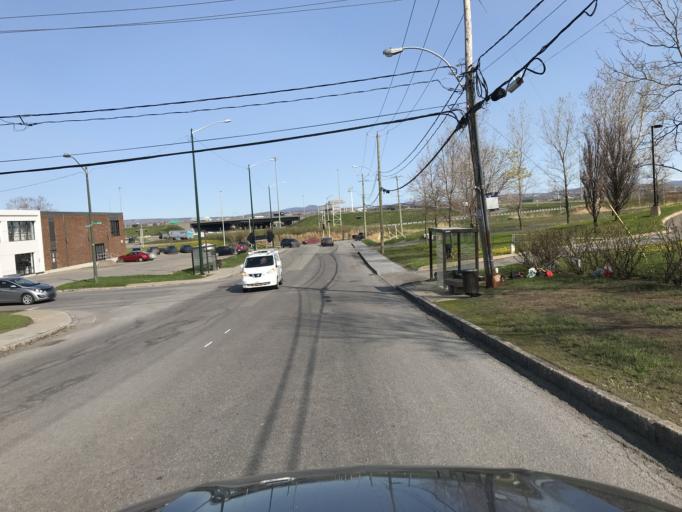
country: CA
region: Quebec
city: L'Ancienne-Lorette
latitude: 46.7917
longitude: -71.2843
